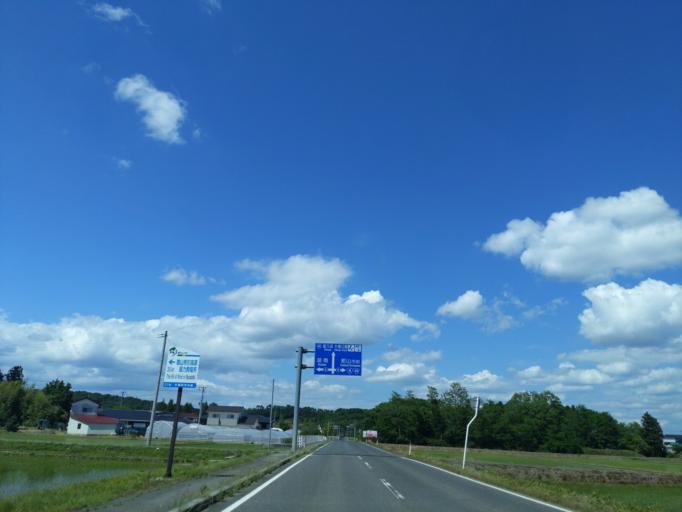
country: JP
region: Fukushima
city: Koriyama
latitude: 37.3875
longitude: 140.3010
